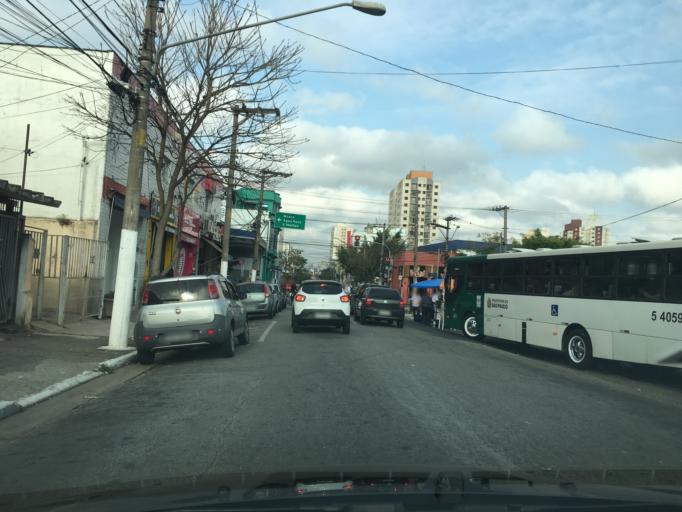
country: BR
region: Sao Paulo
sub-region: Sao Paulo
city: Sao Paulo
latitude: -23.5472
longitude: -46.6068
